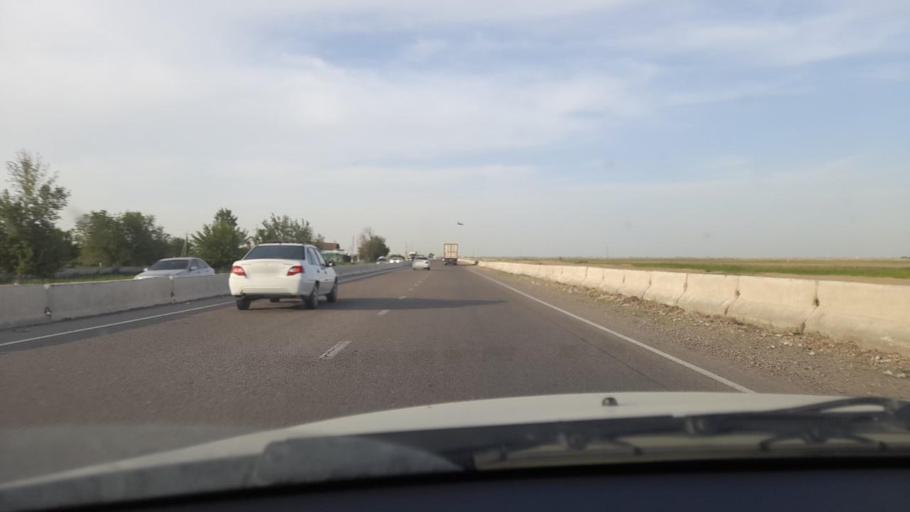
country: UZ
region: Jizzax
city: Dustlik
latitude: 40.4491
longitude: 68.2472
